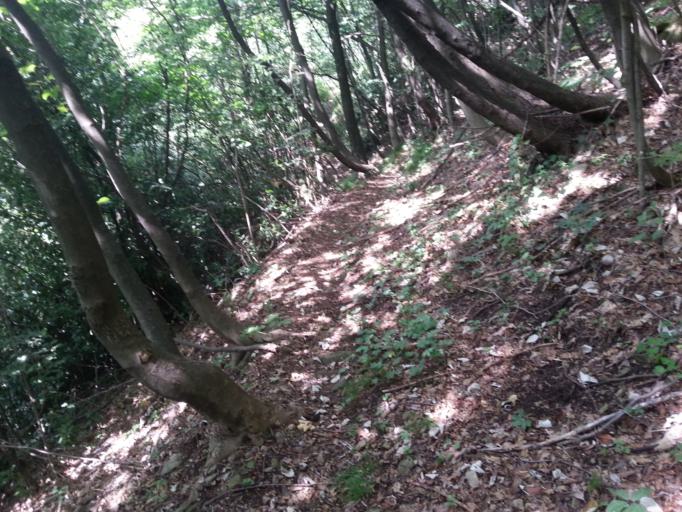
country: IT
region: Lombardy
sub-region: Provincia di Lecco
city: Ballabio
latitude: 45.8836
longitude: 9.4215
